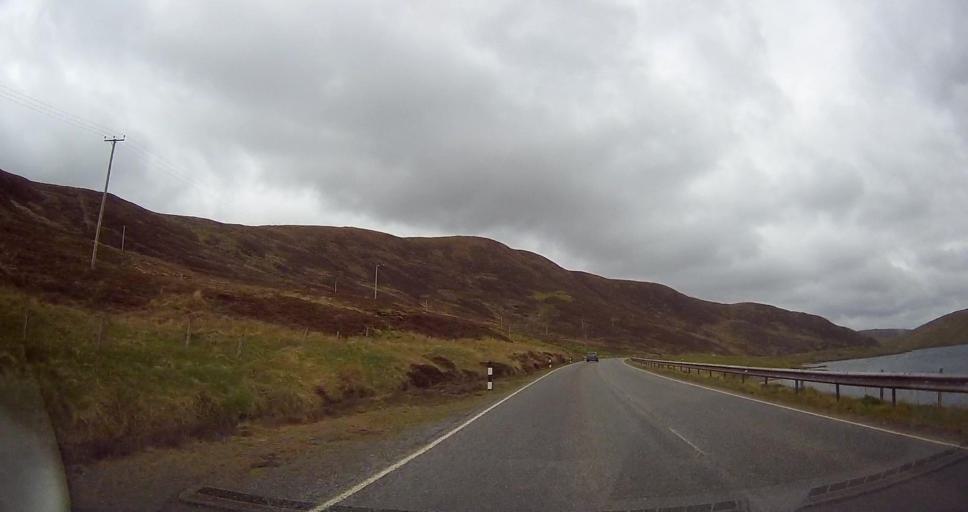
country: GB
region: Scotland
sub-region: Shetland Islands
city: Lerwick
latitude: 60.3686
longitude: -1.2972
